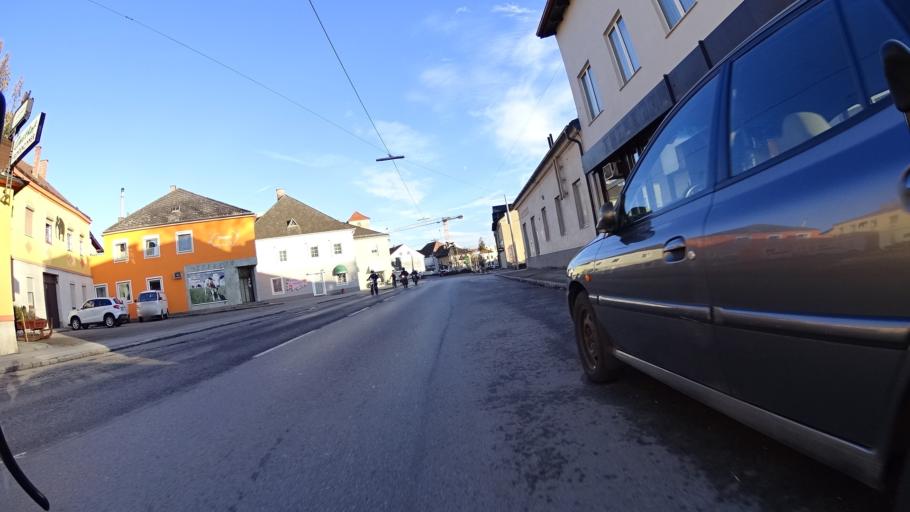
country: AT
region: Lower Austria
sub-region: Politischer Bezirk Korneuburg
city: Stockerau
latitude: 48.3848
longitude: 16.2041
